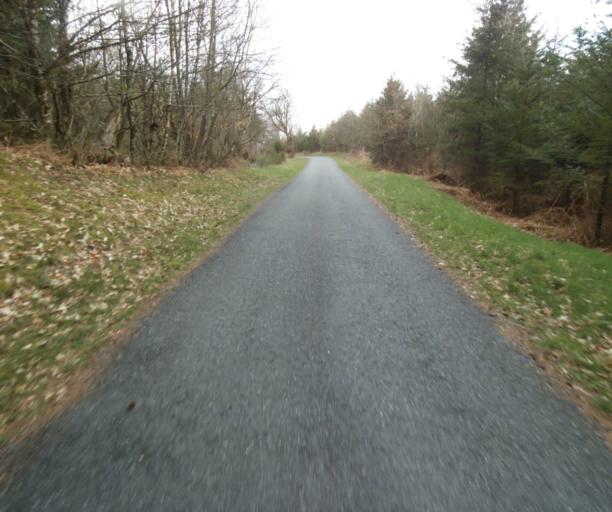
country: FR
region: Limousin
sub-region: Departement de la Correze
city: Correze
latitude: 45.2921
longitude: 1.9256
